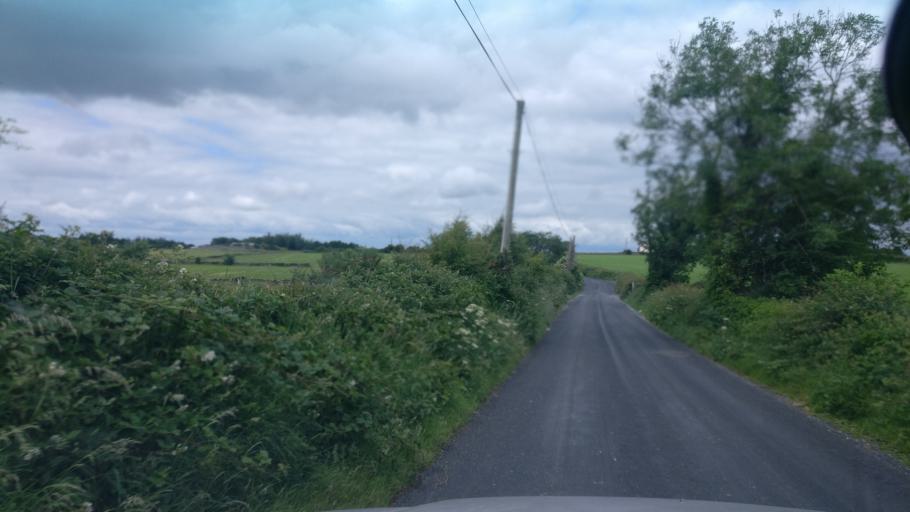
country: IE
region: Connaught
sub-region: County Galway
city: Loughrea
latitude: 53.1650
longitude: -8.5533
